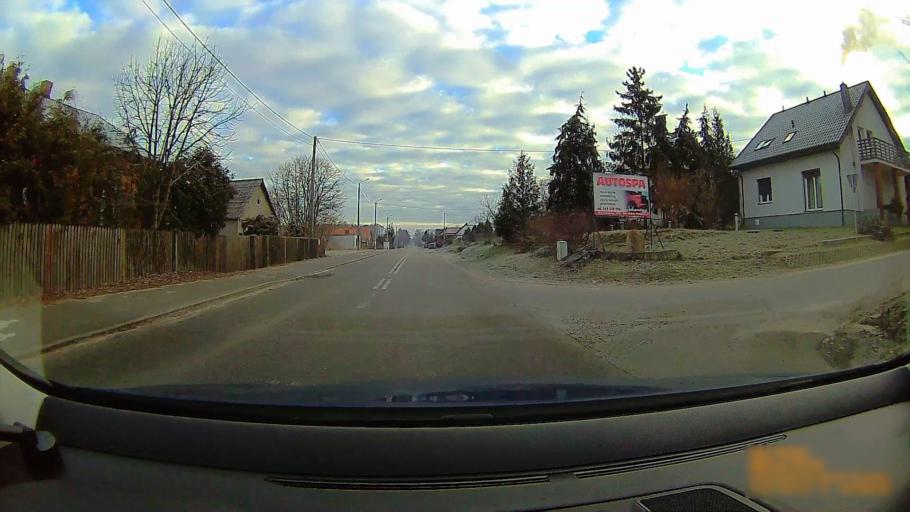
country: PL
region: Greater Poland Voivodeship
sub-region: Powiat koninski
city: Rzgow Pierwszy
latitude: 52.1693
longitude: 18.0853
